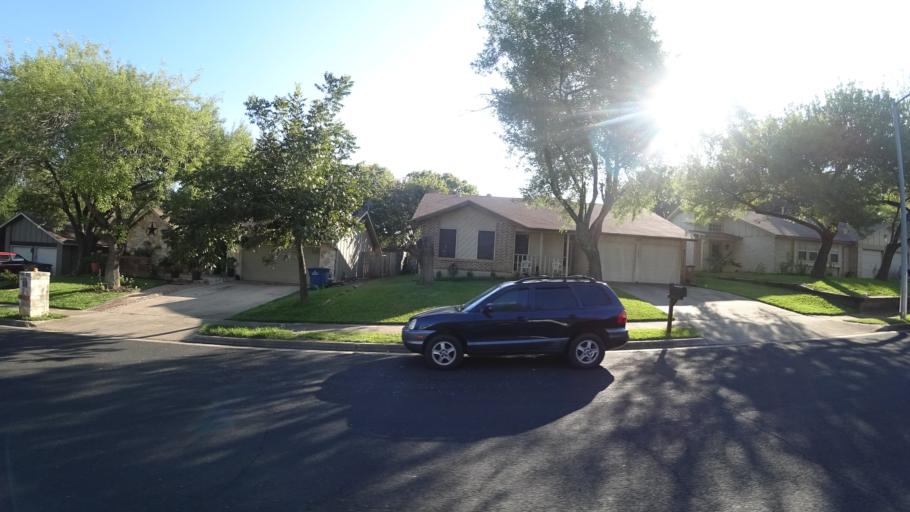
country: US
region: Texas
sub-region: Travis County
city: Wells Branch
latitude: 30.3585
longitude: -97.6766
